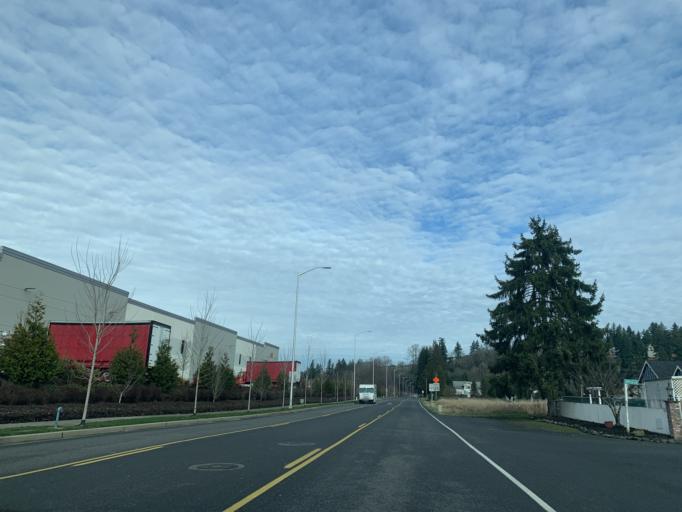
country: US
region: Washington
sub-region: Pierce County
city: Milton
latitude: 47.2232
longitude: -122.3205
